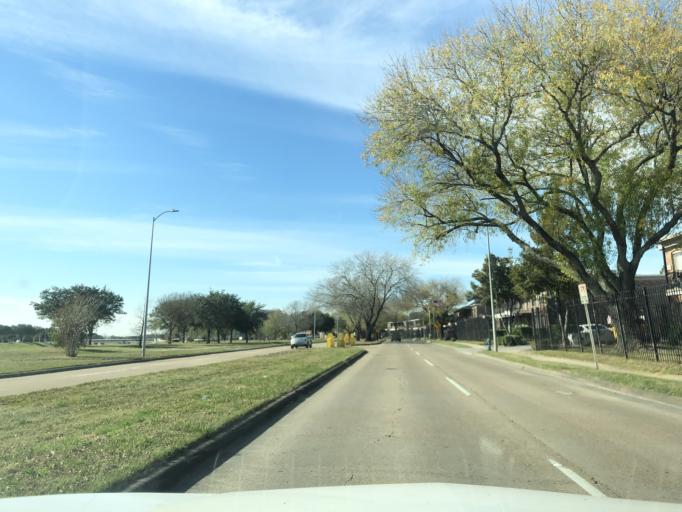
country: US
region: Texas
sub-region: Harris County
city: Bellaire
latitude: 29.6791
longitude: -95.4947
